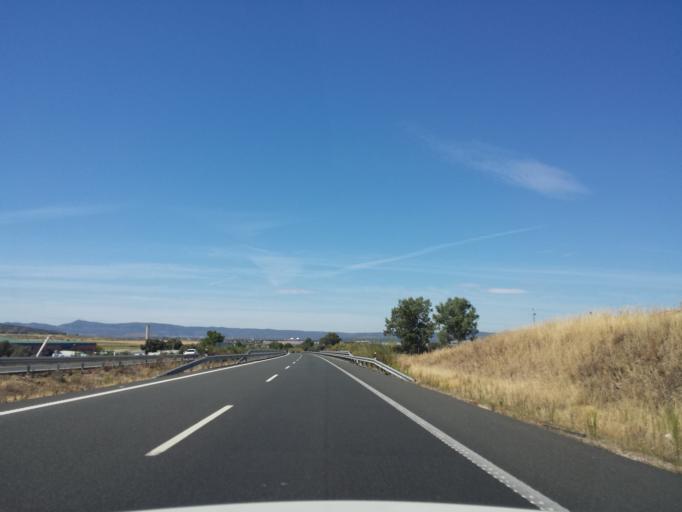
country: ES
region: Extremadura
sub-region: Provincia de Caceres
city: Saucedilla
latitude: 39.8465
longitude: -5.6363
